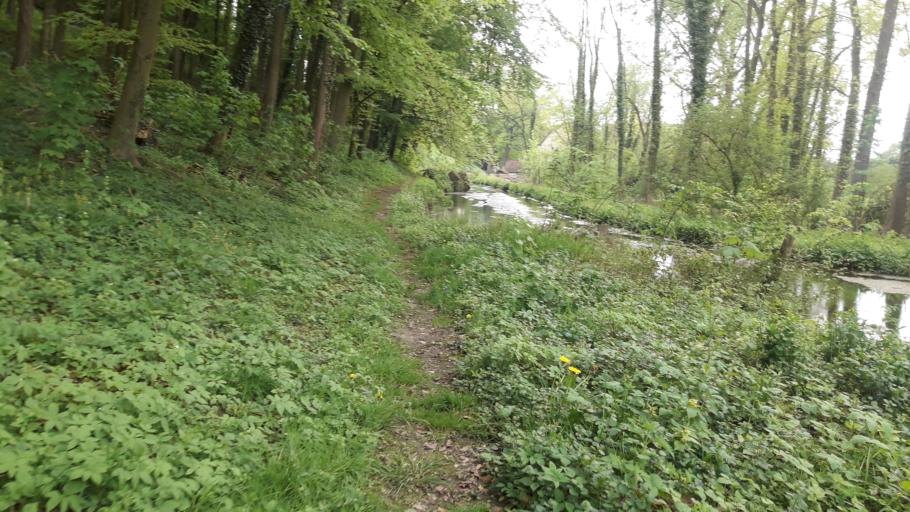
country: DE
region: North Rhine-Westphalia
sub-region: Regierungsbezirk Detmold
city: Paderborn
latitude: 51.6611
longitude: 8.7376
